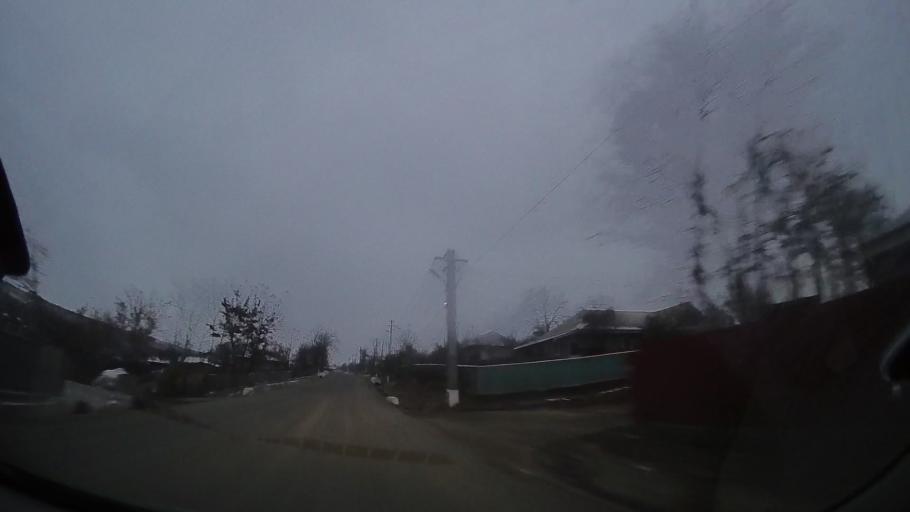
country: RO
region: Vaslui
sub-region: Comuna Gagesti
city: Gagesti
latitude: 46.3906
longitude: 27.9809
